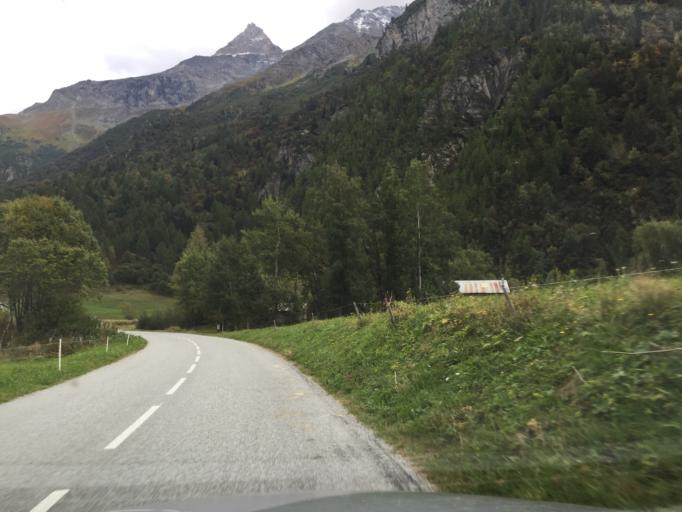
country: FR
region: Rhone-Alpes
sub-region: Departement de la Savoie
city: Belle-Plagne
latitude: 45.5200
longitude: 6.7978
